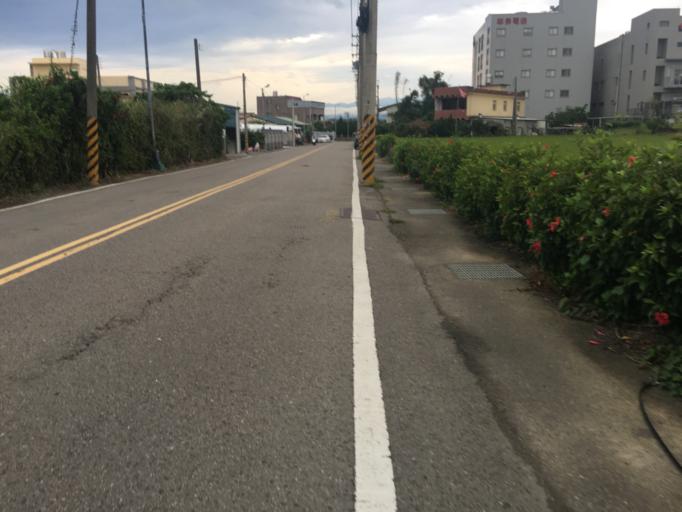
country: TW
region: Taiwan
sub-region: Hsinchu
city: Hsinchu
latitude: 24.7294
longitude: 120.9103
